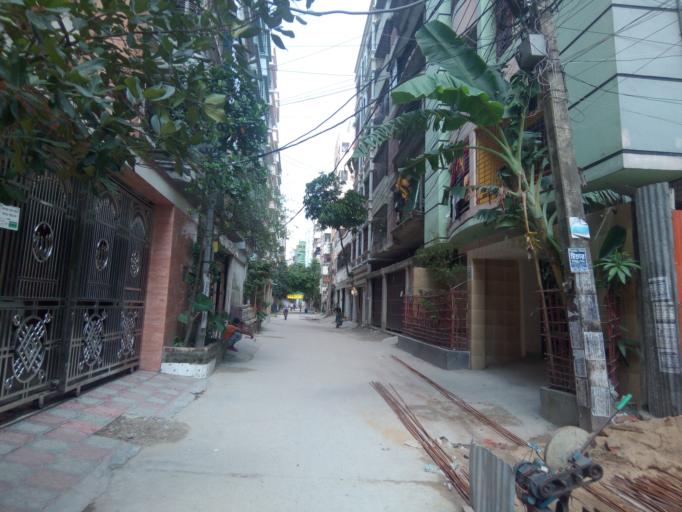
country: BD
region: Dhaka
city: Paltan
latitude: 23.7609
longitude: 90.4347
